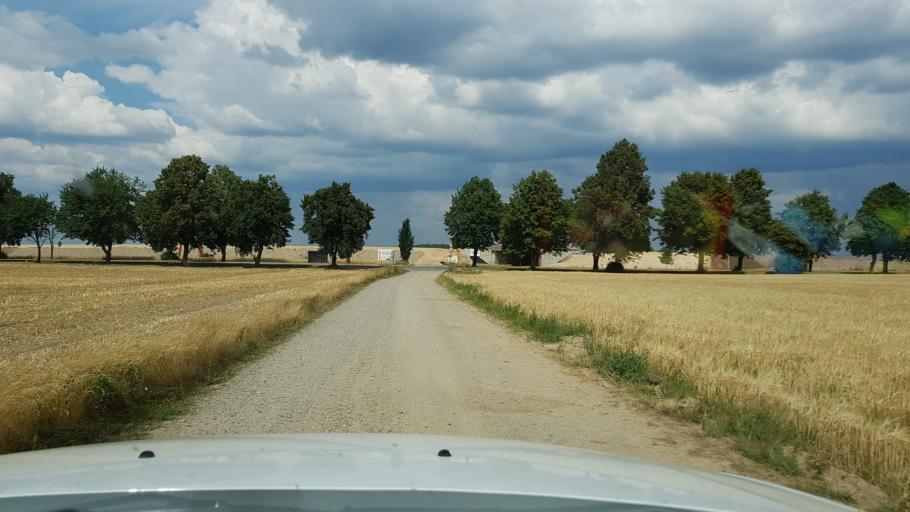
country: PL
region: West Pomeranian Voivodeship
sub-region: Powiat walecki
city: Walcz
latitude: 53.2528
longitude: 16.5162
